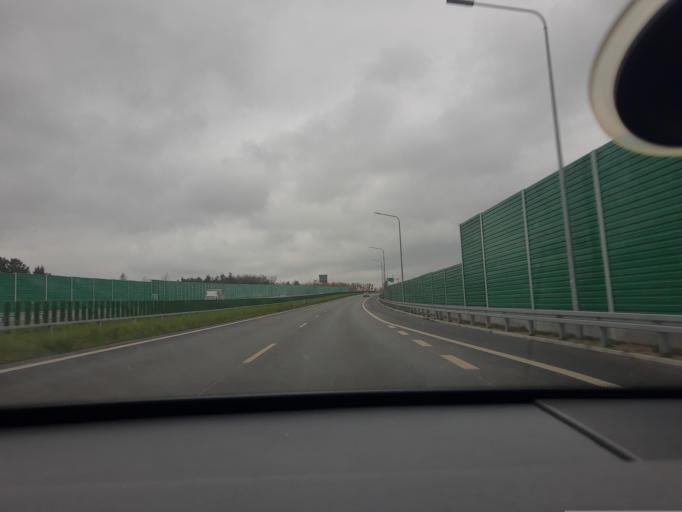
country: PL
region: Lodz Voivodeship
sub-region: Powiat pabianicki
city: Konstantynow Lodzki
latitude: 51.7249
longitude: 19.3566
